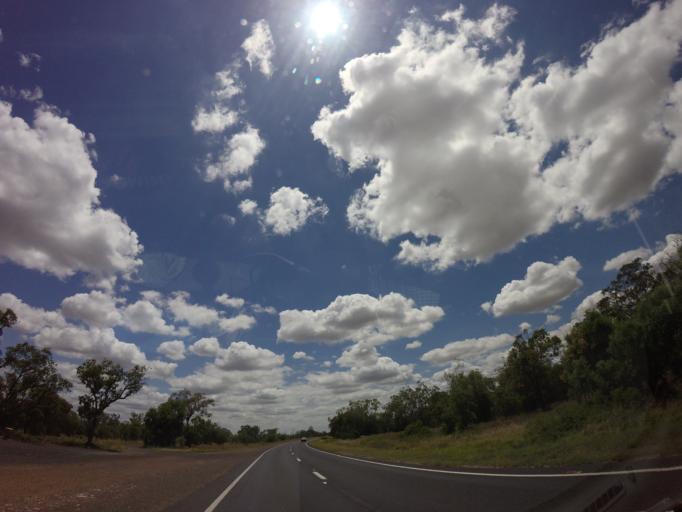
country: AU
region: New South Wales
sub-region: Moree Plains
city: Boggabilla
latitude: -28.7357
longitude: 150.2683
